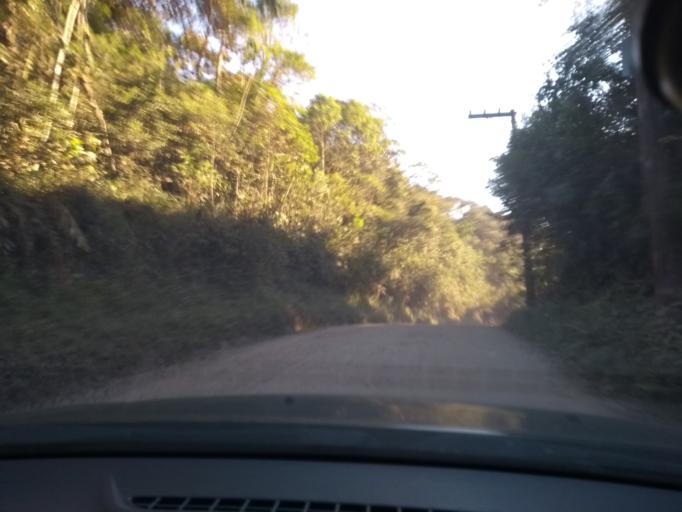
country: BR
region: Sao Paulo
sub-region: Sao Bernardo Do Campo
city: Sao Bernardo do Campo
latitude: -23.7746
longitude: -46.5014
